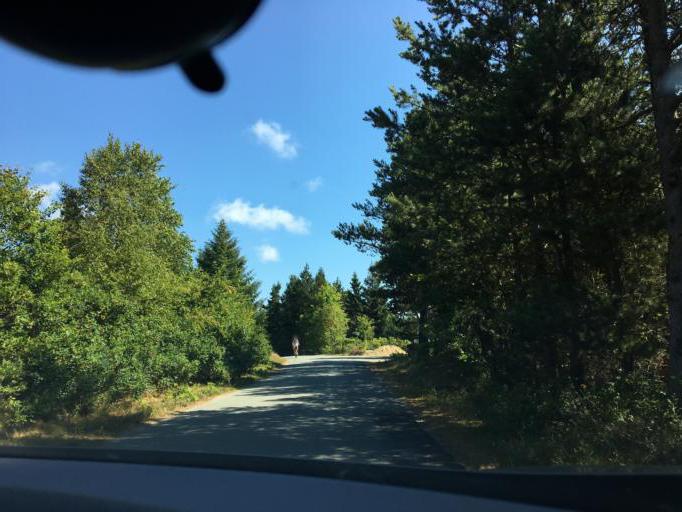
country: DK
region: South Denmark
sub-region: Varde Kommune
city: Oksbol
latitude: 55.7342
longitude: 8.2053
